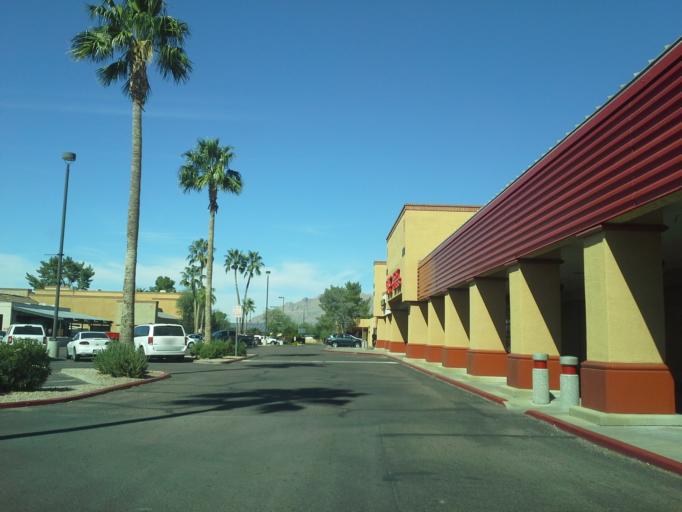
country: US
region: Arizona
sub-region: Pima County
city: Tucson
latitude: 32.2596
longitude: -110.9428
